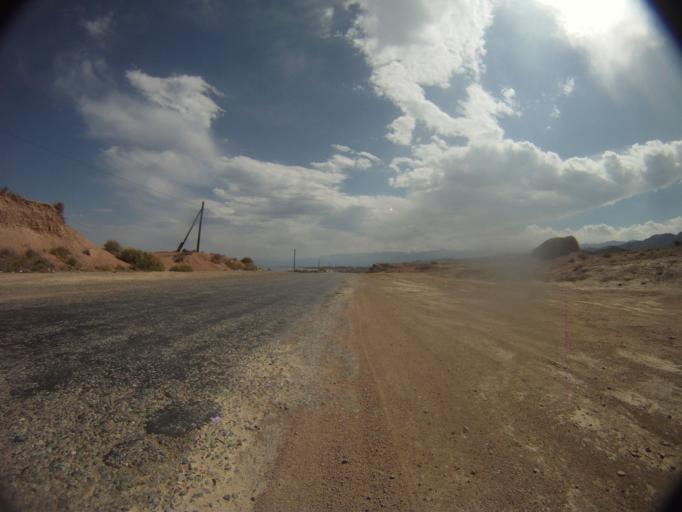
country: KG
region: Ysyk-Koel
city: Kadzhi-Say
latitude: 42.1759
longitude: 77.3467
